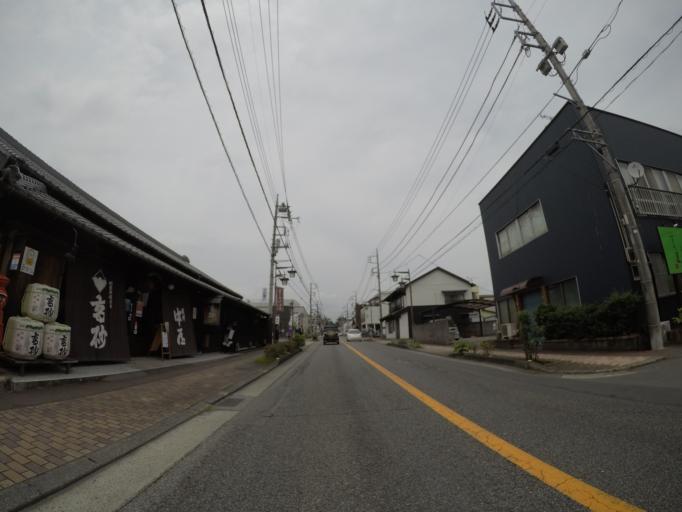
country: JP
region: Shizuoka
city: Fujinomiya
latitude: 35.2284
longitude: 138.6067
